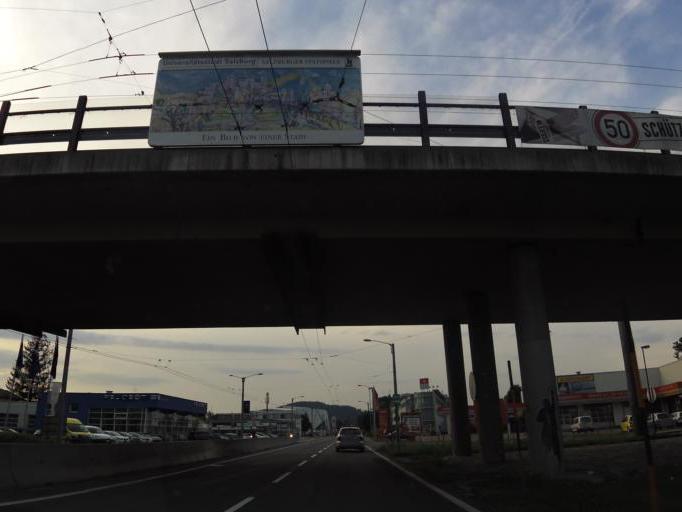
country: AT
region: Salzburg
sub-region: Politischer Bezirk Salzburg-Umgebung
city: Anif
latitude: 47.7707
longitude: 13.0704
